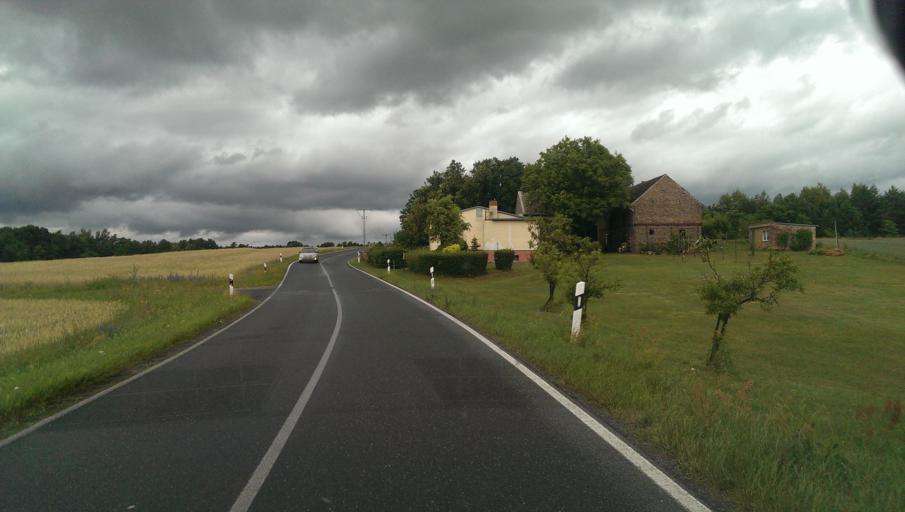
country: DE
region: Brandenburg
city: Golzow
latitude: 52.3582
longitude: 12.6288
